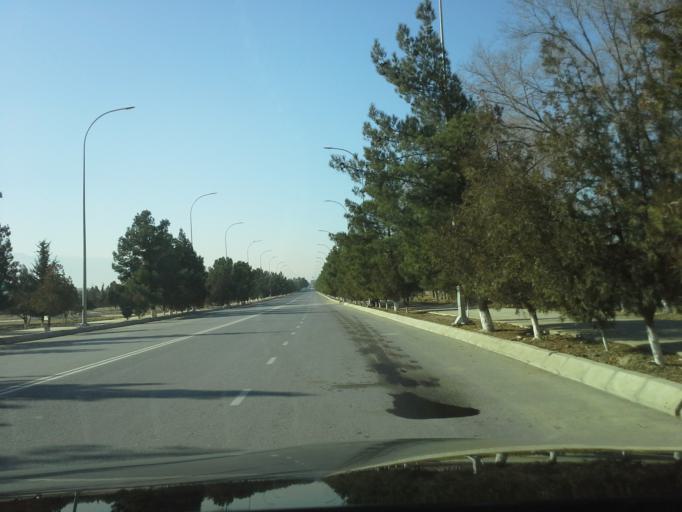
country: TM
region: Ahal
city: Annau
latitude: 37.9059
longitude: 58.4970
